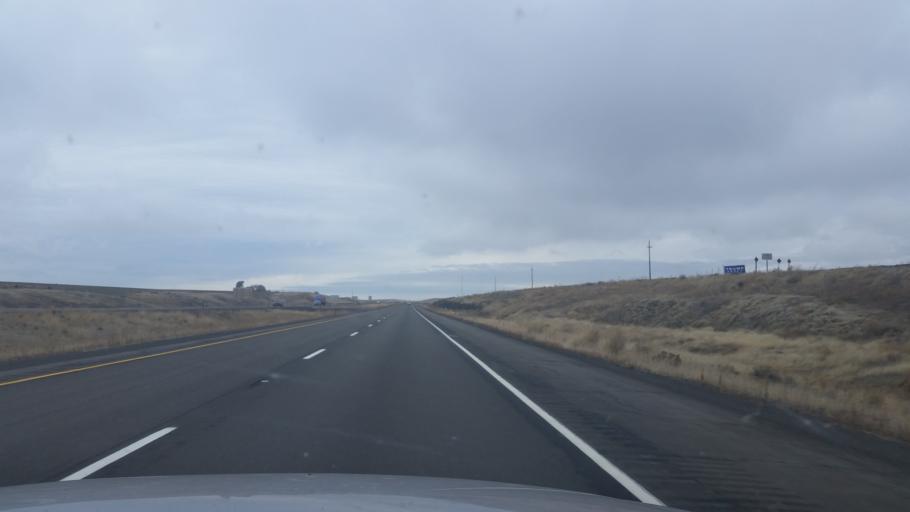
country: US
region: Washington
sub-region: Adams County
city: Ritzville
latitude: 47.1113
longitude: -118.4181
